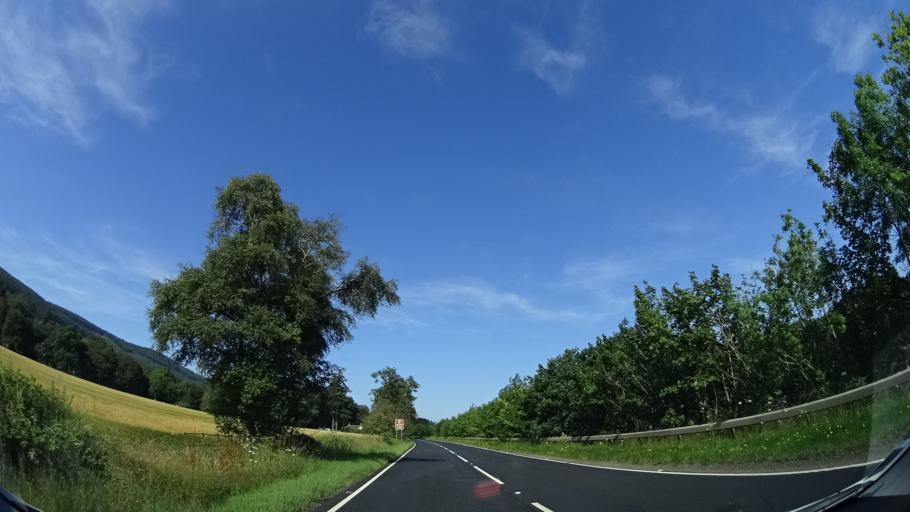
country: GB
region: Scotland
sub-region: Highland
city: Inverness
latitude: 57.4263
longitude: -4.3124
